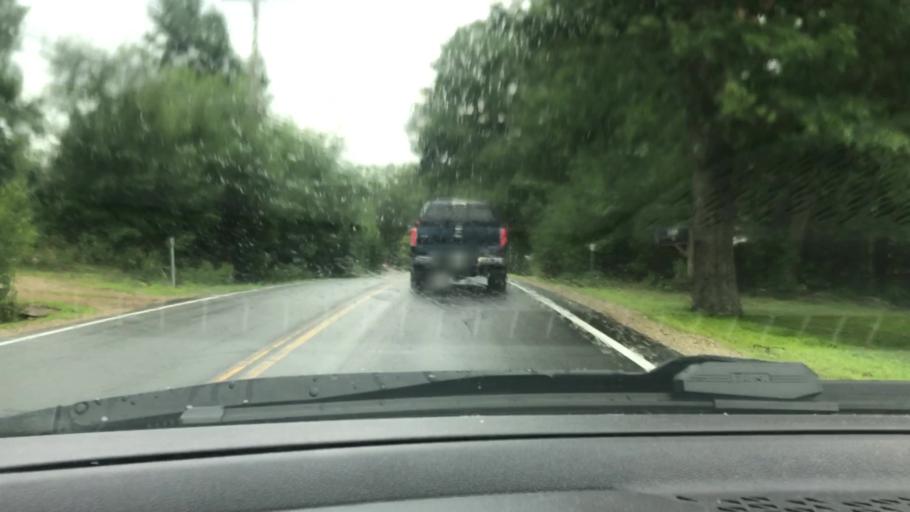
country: US
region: New Hampshire
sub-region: Rockingham County
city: Candia
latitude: 43.1675
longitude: -71.2494
